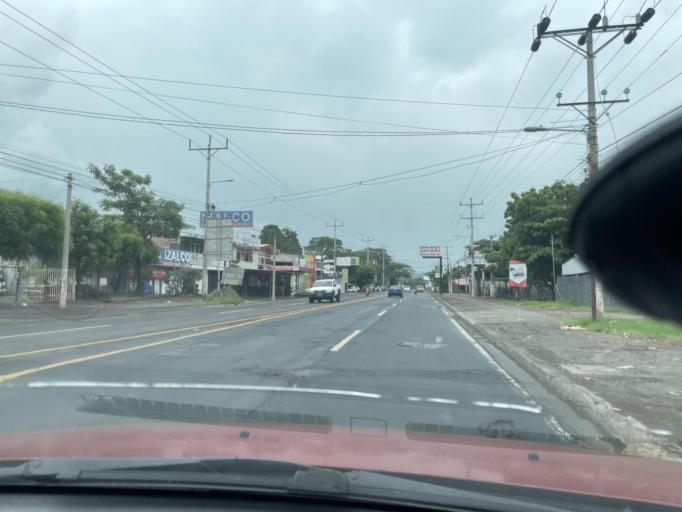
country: SV
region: San Miguel
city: San Miguel
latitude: 13.4966
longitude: -88.1709
